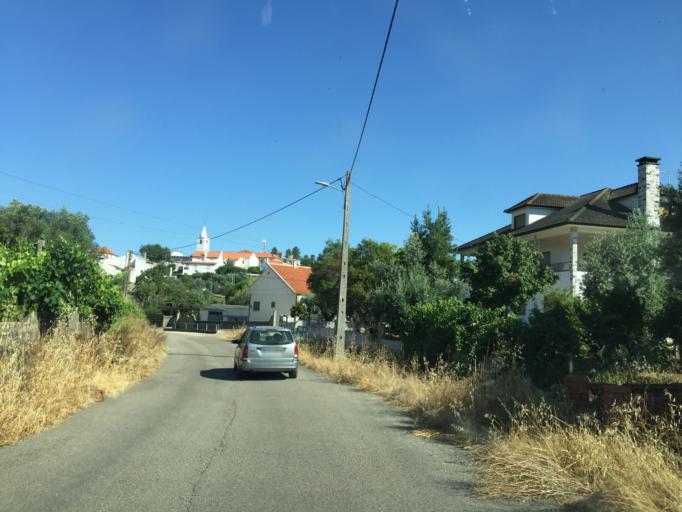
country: PT
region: Santarem
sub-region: Tomar
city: Tomar
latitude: 39.6074
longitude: -8.3313
